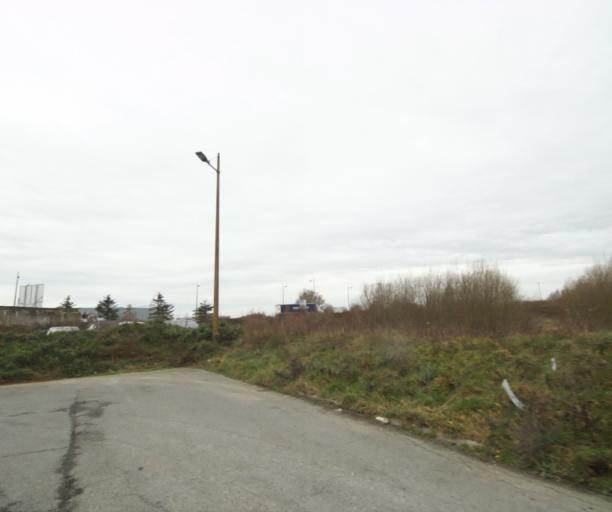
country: FR
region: Nord-Pas-de-Calais
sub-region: Departement du Nord
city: Quarouble
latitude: 50.3808
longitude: 3.6133
